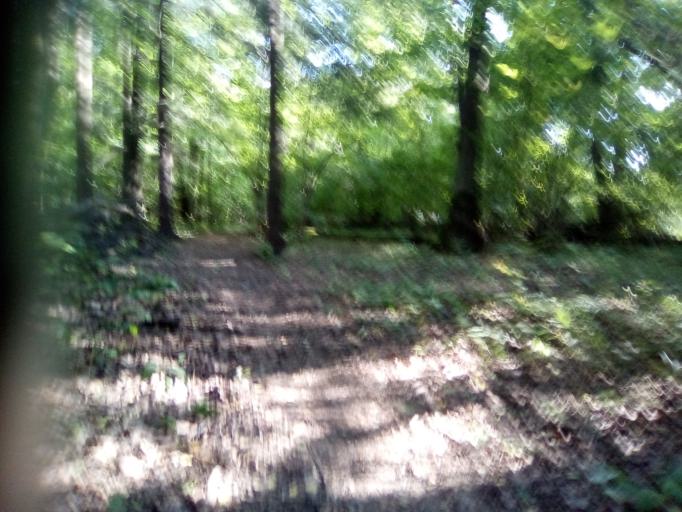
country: RU
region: Moskovskaya
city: Kokoshkino
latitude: 55.6147
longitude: 37.1752
